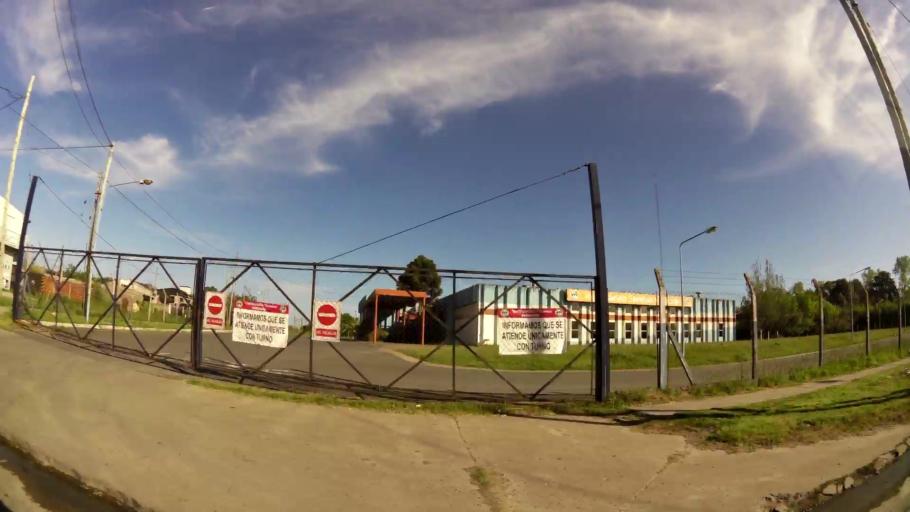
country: AR
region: Buenos Aires
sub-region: Partido de Quilmes
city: Quilmes
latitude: -34.7908
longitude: -58.2196
